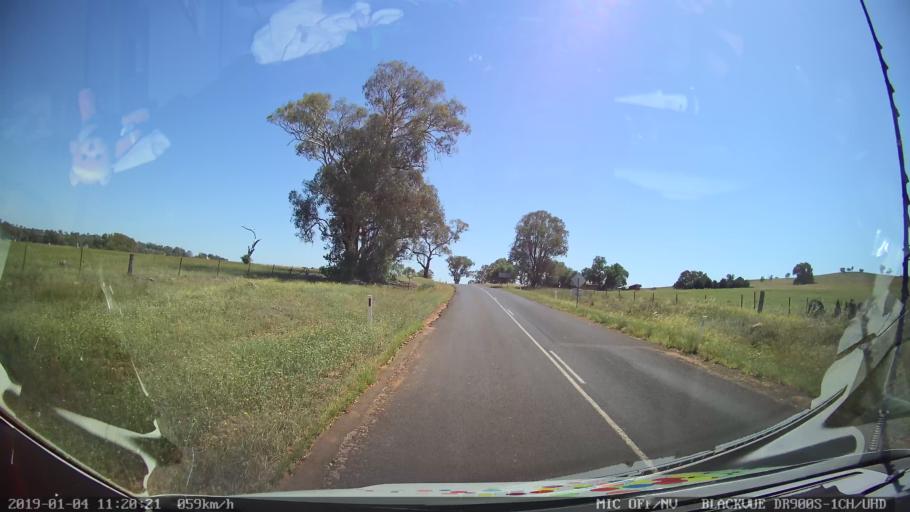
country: AU
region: New South Wales
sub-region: Cabonne
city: Molong
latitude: -33.1646
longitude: 148.7064
